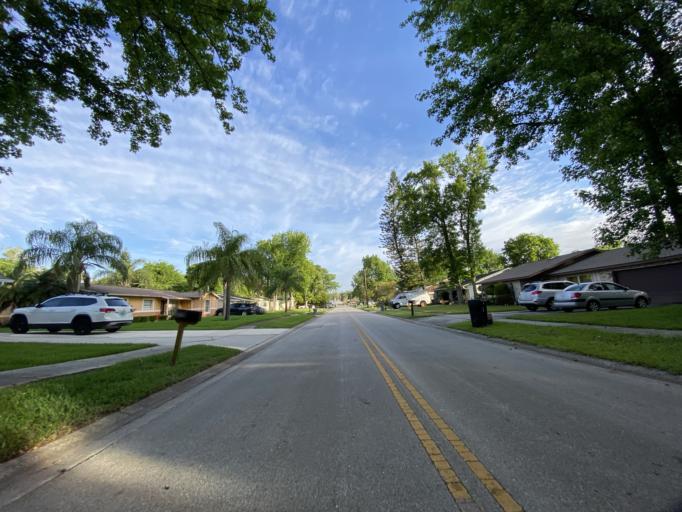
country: US
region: Florida
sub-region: Volusia County
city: South Daytona
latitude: 29.1773
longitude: -81.0160
